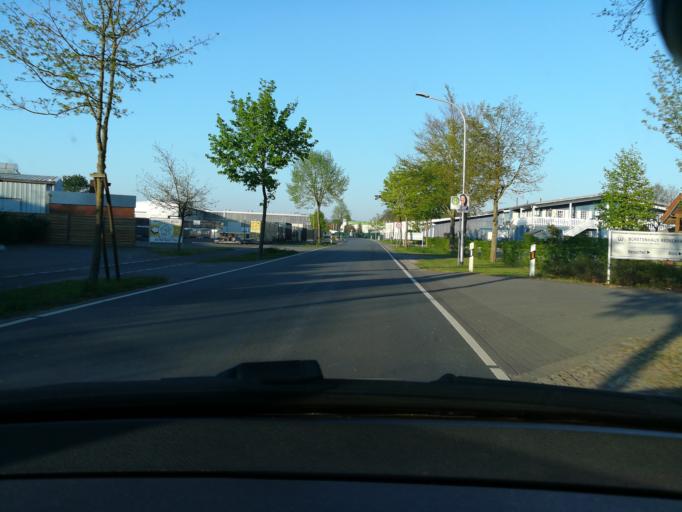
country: DE
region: Lower Saxony
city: Dissen
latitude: 52.0693
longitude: 8.1939
